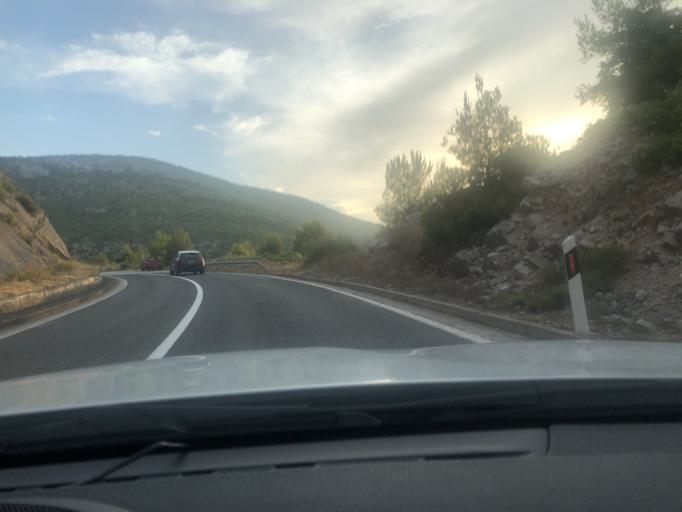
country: HR
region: Splitsko-Dalmatinska
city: Stari Grad
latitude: 43.1678
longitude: 16.5612
